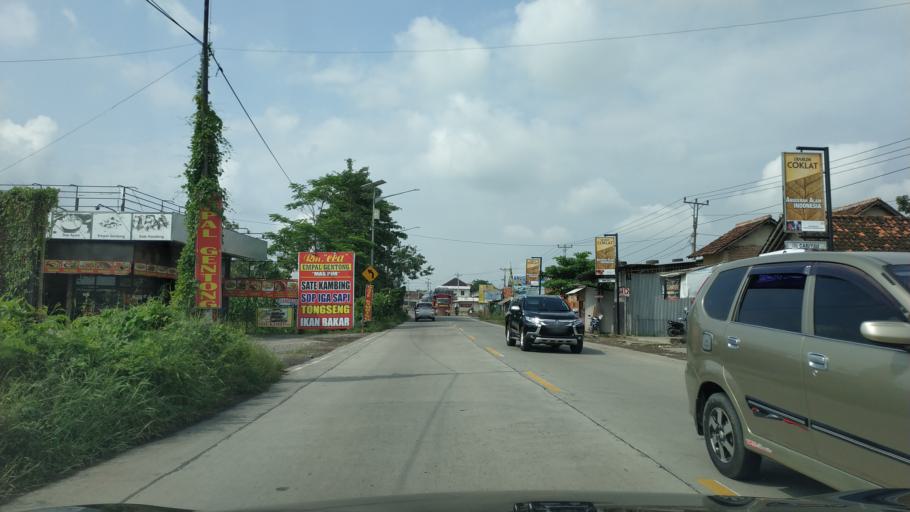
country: ID
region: Central Java
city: Ketanggungan
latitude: -6.8962
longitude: 108.8866
